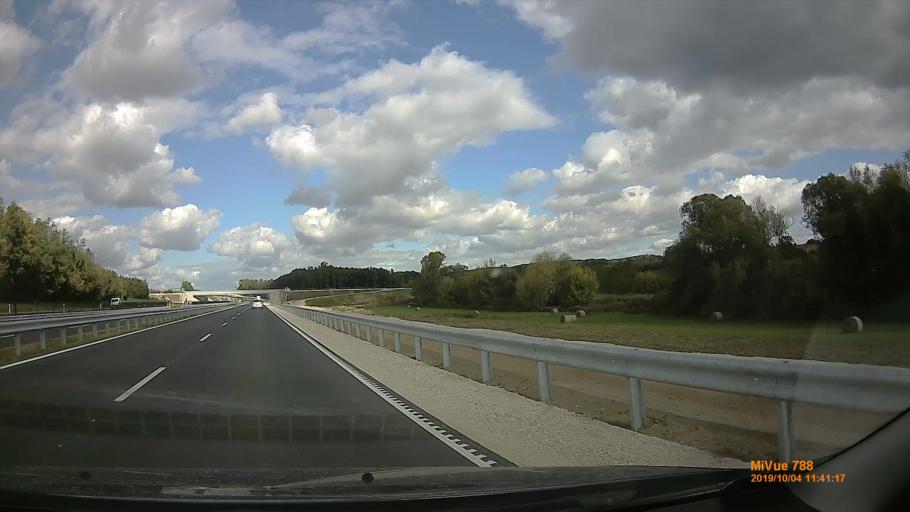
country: HU
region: Somogy
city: Karad
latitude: 46.5757
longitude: 17.8061
